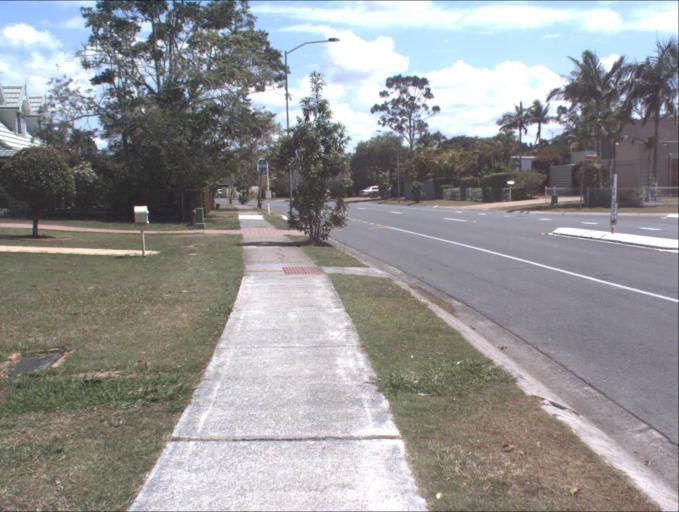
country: AU
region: Queensland
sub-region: Logan
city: Slacks Creek
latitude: -27.6675
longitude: 153.1470
